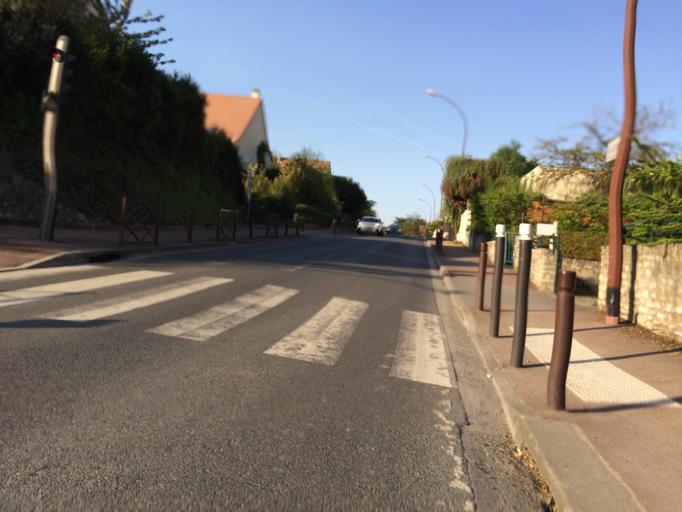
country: FR
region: Ile-de-France
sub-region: Departement des Hauts-de-Seine
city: Chatenay-Malabry
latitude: 48.7566
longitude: 2.2762
